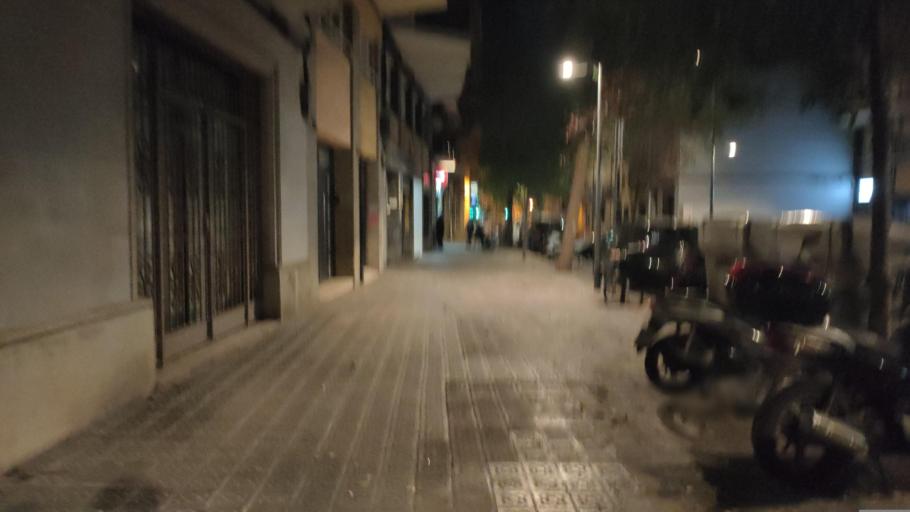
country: ES
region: Catalonia
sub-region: Provincia de Barcelona
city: Horta-Guinardo
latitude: 41.4141
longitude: 2.1817
